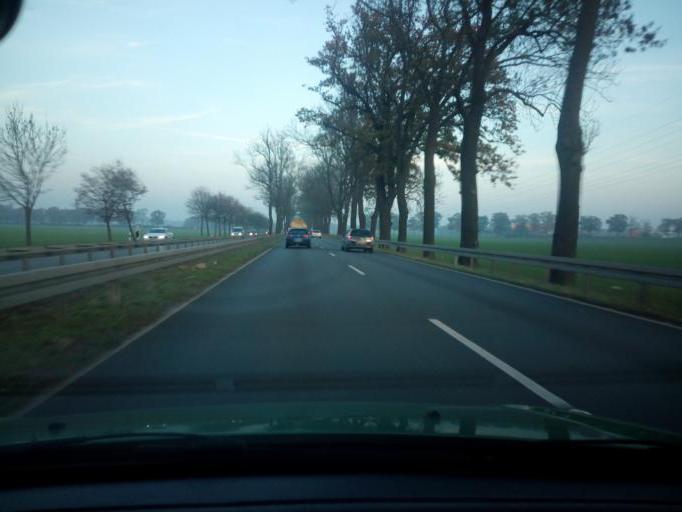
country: DE
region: Brandenburg
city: Schoneiche
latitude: 52.5008
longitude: 13.6939
